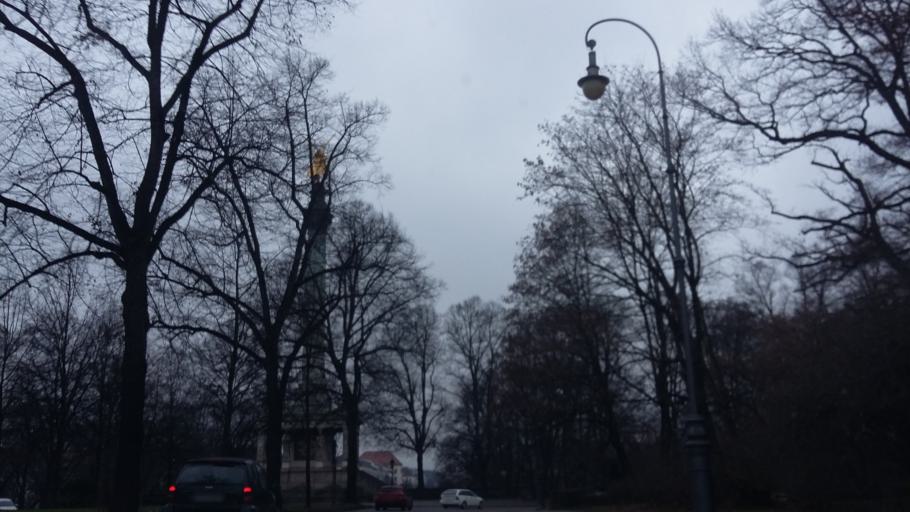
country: DE
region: Bavaria
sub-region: Upper Bavaria
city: Bogenhausen
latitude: 48.1413
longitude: 11.5984
